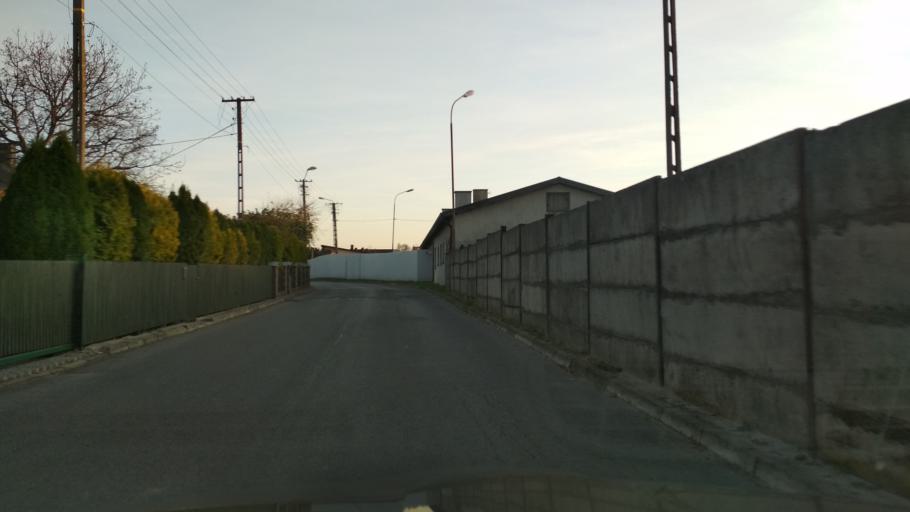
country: PL
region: Subcarpathian Voivodeship
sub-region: Powiat ropczycko-sedziszowski
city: Sedziszow Malopolski
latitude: 50.0666
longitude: 21.7102
